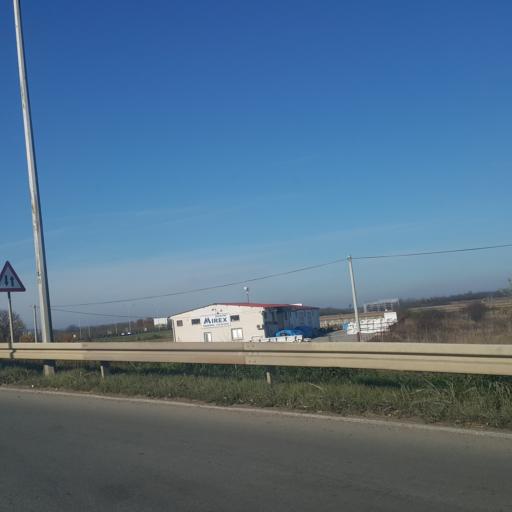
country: RS
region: Central Serbia
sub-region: Sumadijski Okrug
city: Lapovo
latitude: 44.2378
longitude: 21.1201
